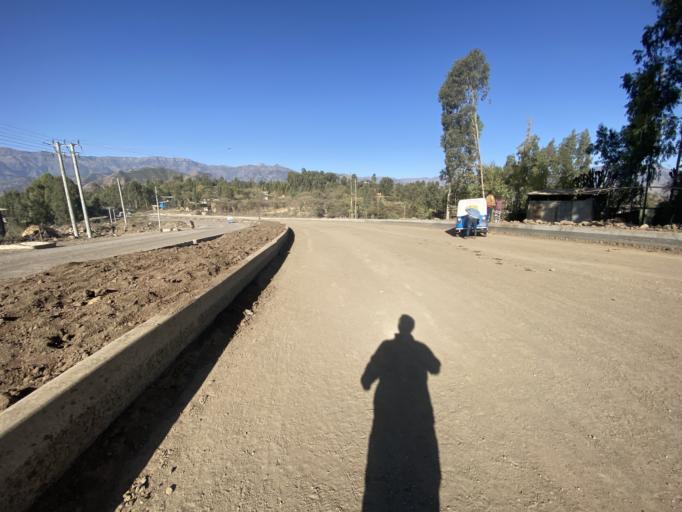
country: ET
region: Amhara
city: Robit
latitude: 11.8279
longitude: 39.5691
